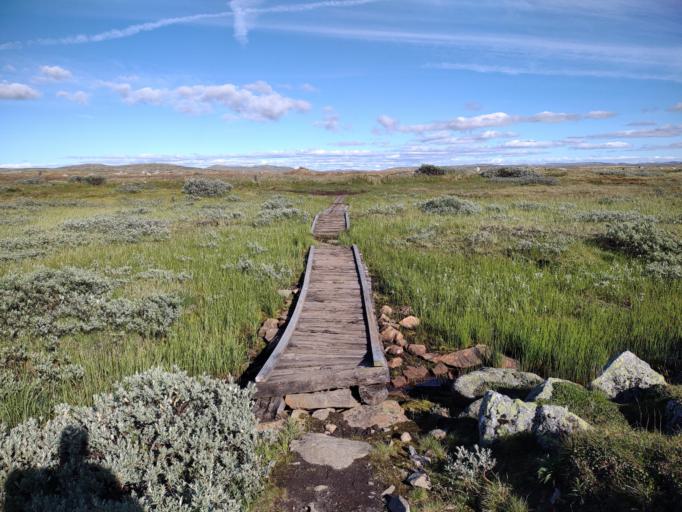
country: NO
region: Hordaland
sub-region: Eidfjord
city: Eidfjord
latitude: 60.1754
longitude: 7.4649
